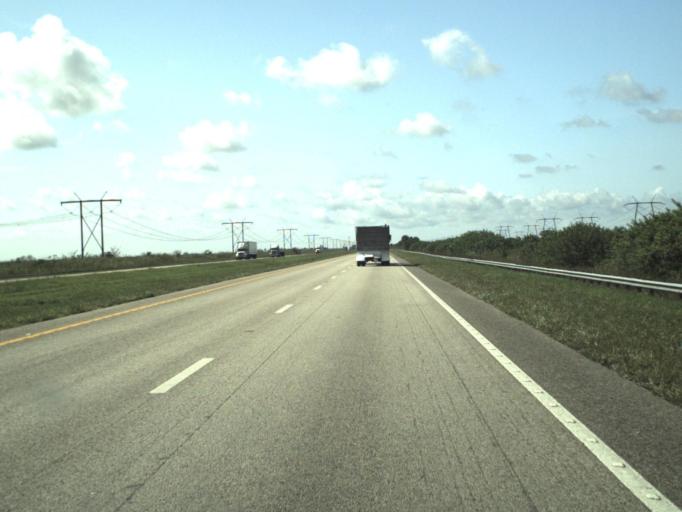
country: US
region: Florida
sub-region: Broward County
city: Weston
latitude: 26.2166
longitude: -80.4577
